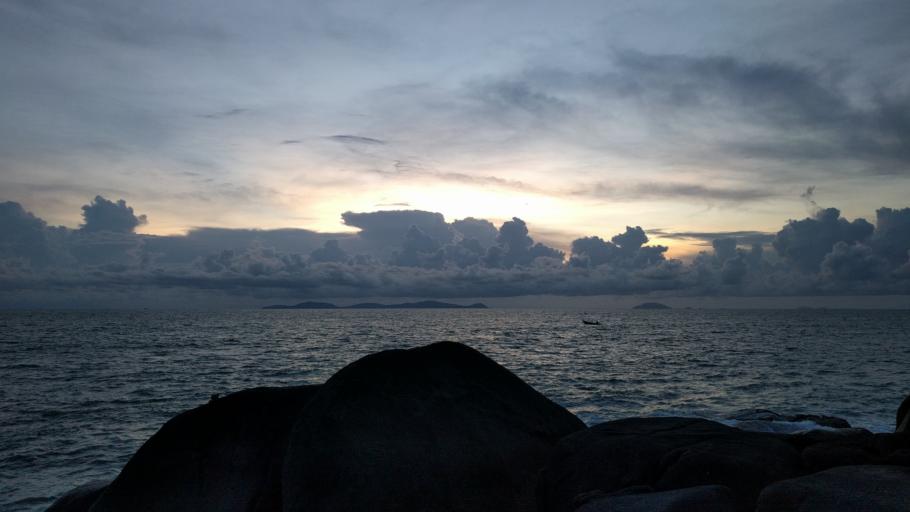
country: MM
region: Tanintharyi
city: Dawei
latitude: 14.0870
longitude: 98.0695
